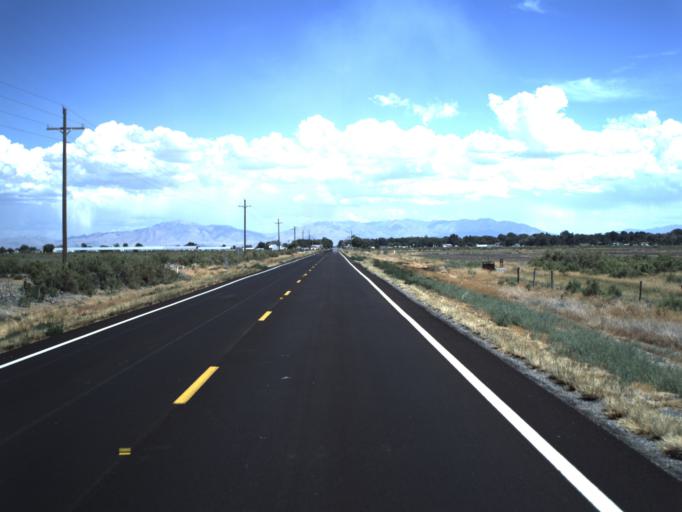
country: US
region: Utah
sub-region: Millard County
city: Delta
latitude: 39.3308
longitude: -112.6910
